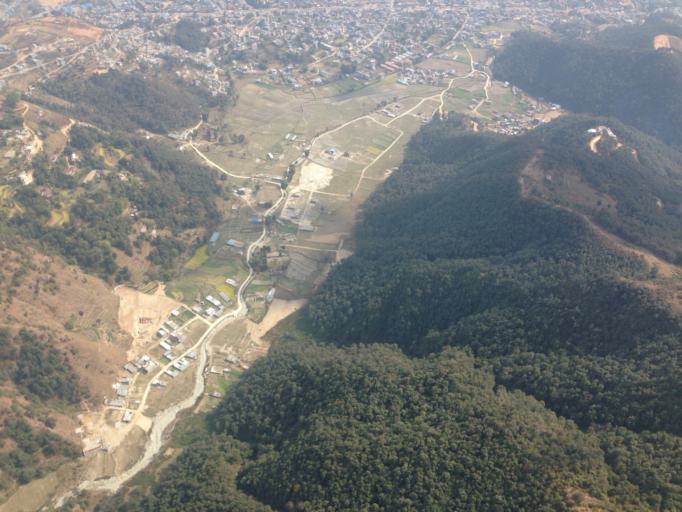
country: NP
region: Western Region
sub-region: Gandaki Zone
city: Pokhara
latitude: 28.2405
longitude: 83.9659
